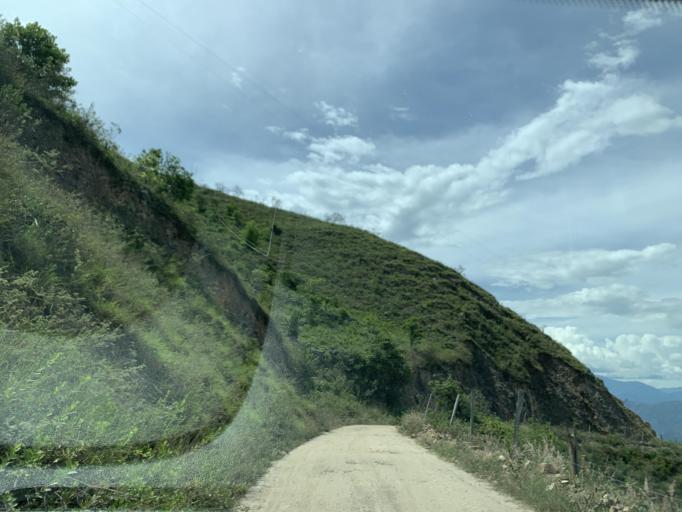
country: CO
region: Boyaca
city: Tipacoque
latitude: 6.4485
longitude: -72.7066
